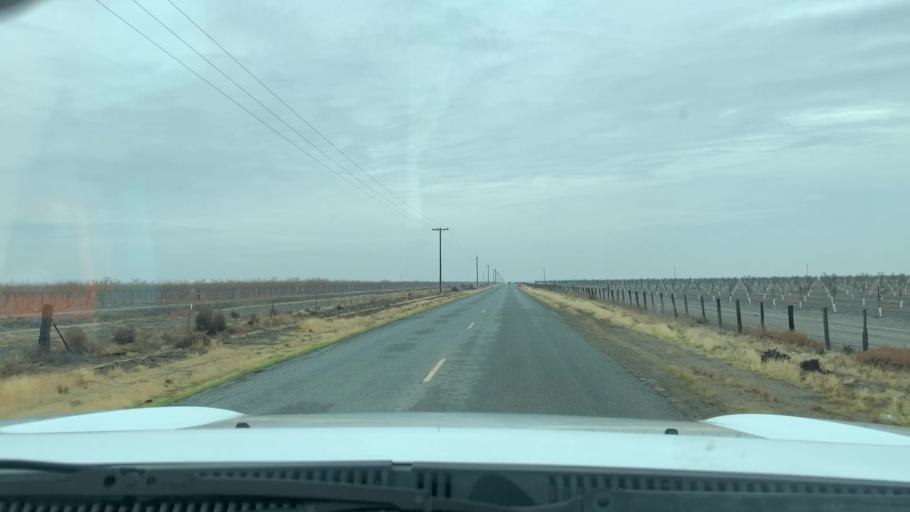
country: US
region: California
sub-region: Tulare County
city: Alpaugh
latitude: 35.7608
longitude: -119.5703
